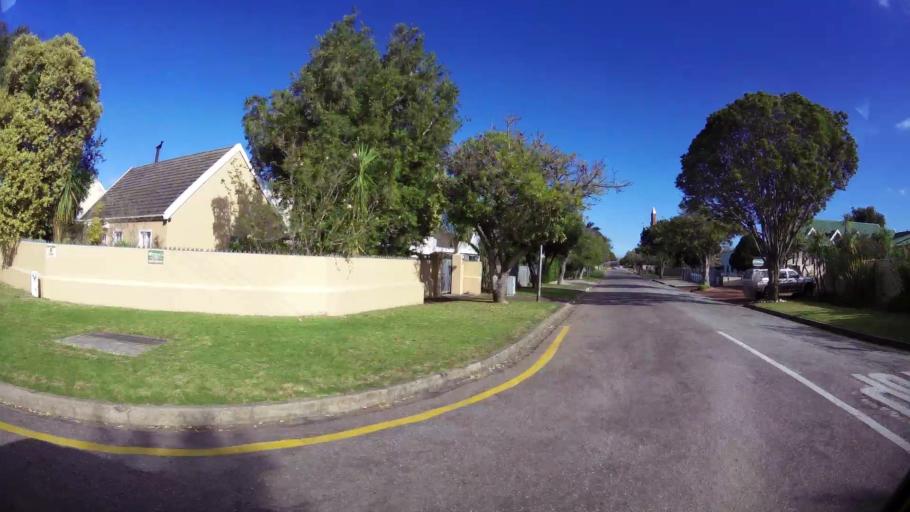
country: ZA
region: Western Cape
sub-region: Eden District Municipality
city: George
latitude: -33.9597
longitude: 22.4859
